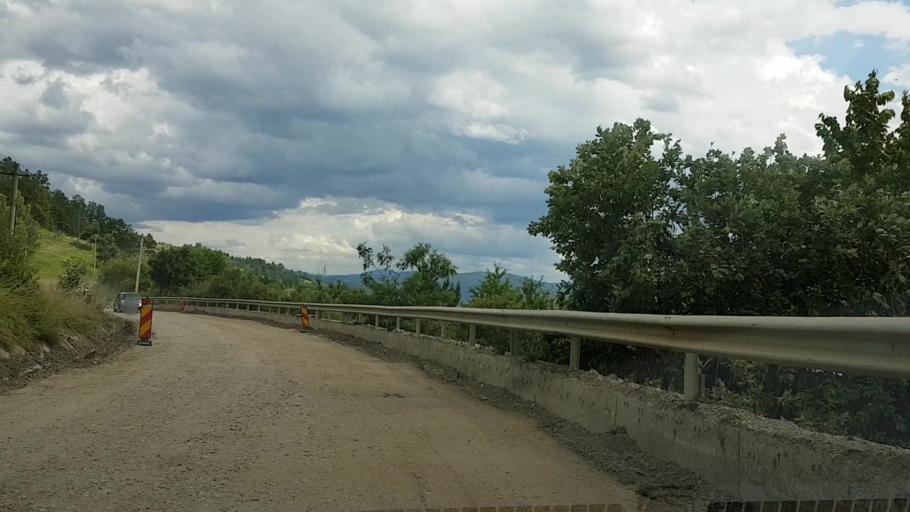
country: RO
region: Neamt
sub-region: Comuna Hangu
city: Hangu
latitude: 47.0392
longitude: 26.0575
